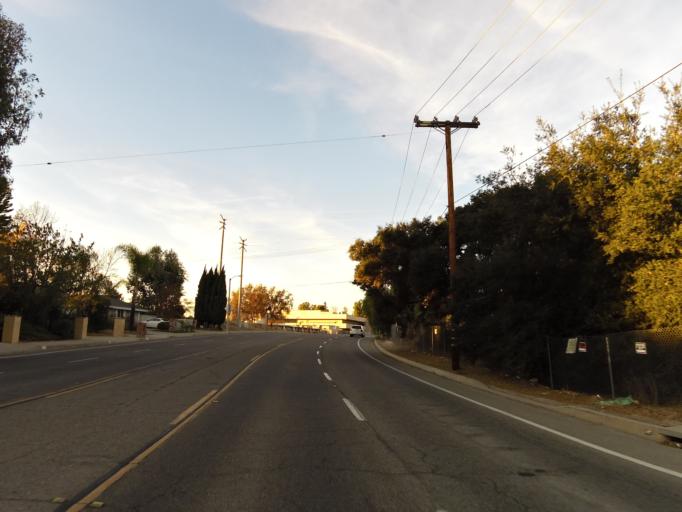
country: US
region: California
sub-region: Ventura County
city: Thousand Oaks
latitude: 34.2051
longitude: -118.8393
